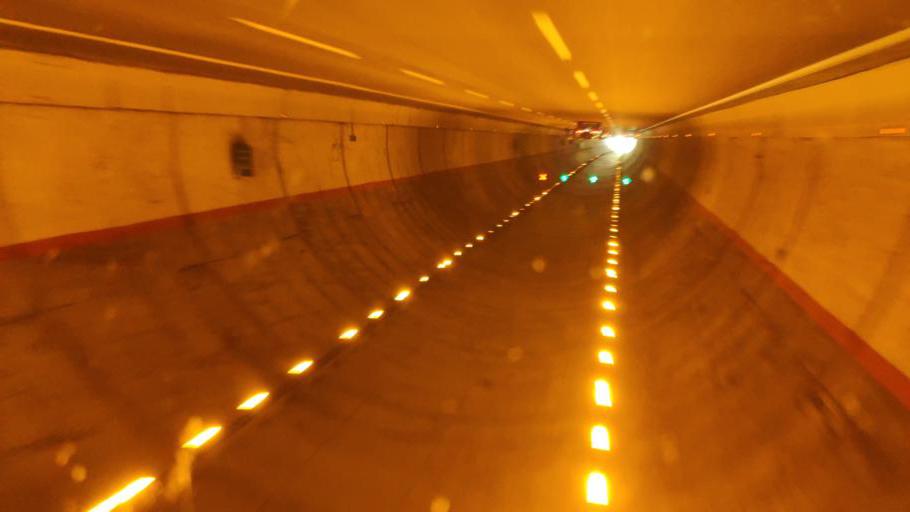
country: IT
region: Campania
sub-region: Provincia di Salerno
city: Piegolelle-San Bartolomeo
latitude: 40.6990
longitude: 14.8165
